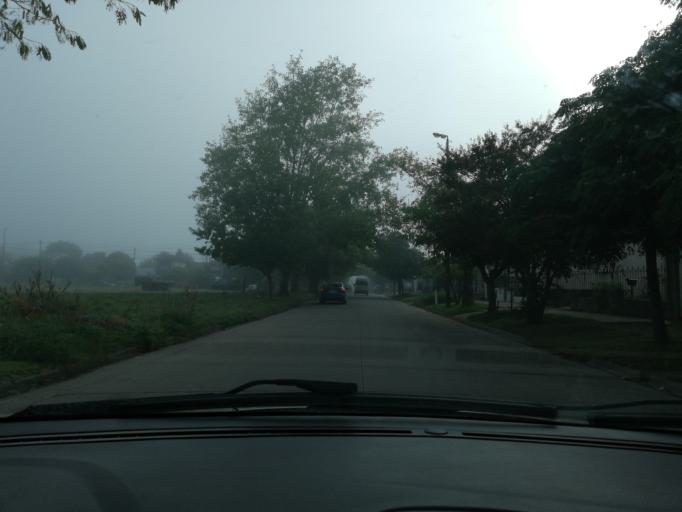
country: AR
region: Buenos Aires
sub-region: Partido de Balcarce
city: Balcarce
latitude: -37.8432
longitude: -58.2494
